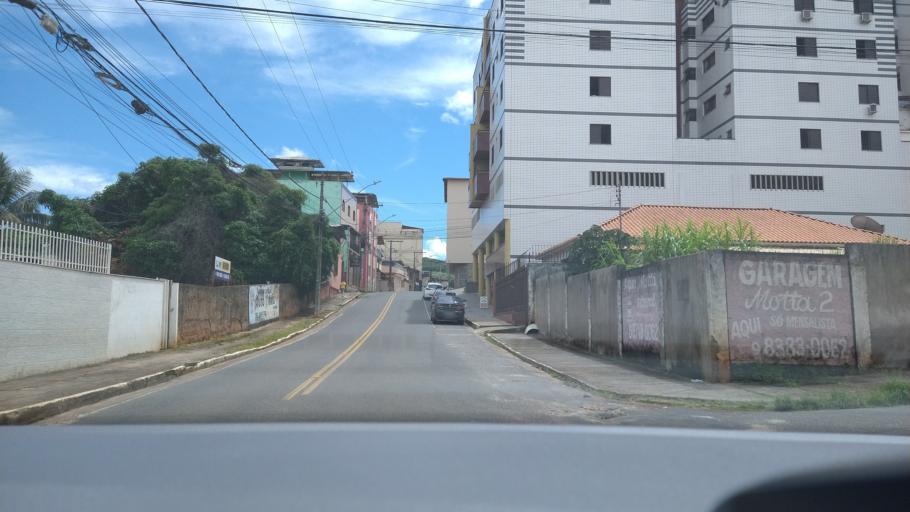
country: BR
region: Minas Gerais
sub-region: Vicosa
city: Vicosa
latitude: -20.7628
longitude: -42.8829
